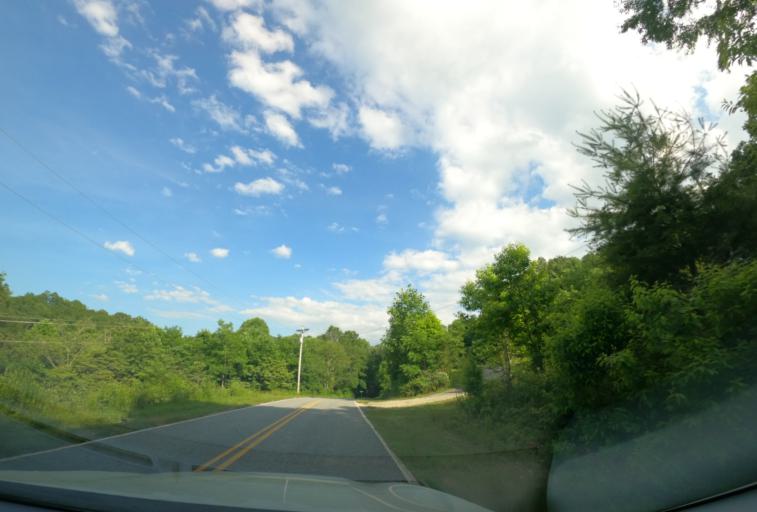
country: US
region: North Carolina
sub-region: Transylvania County
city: Brevard
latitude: 35.2341
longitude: -82.8591
